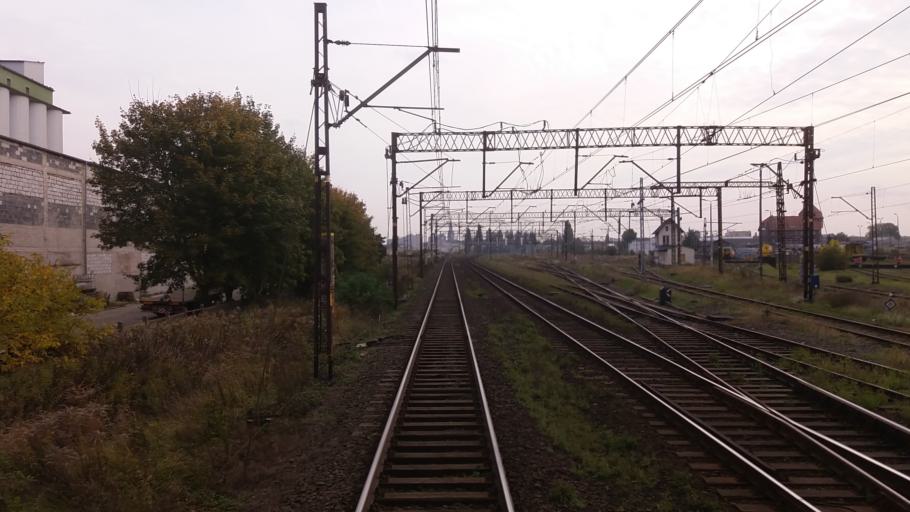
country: PL
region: West Pomeranian Voivodeship
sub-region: Powiat stargardzki
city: Stargard Szczecinski
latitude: 53.3505
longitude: 15.0182
